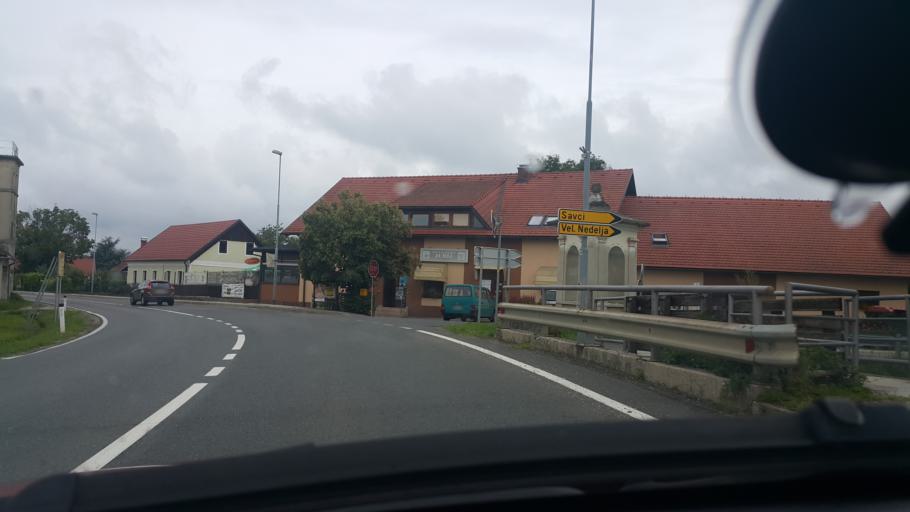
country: SI
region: Ormoz
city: Ormoz
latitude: 46.4160
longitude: 16.1112
